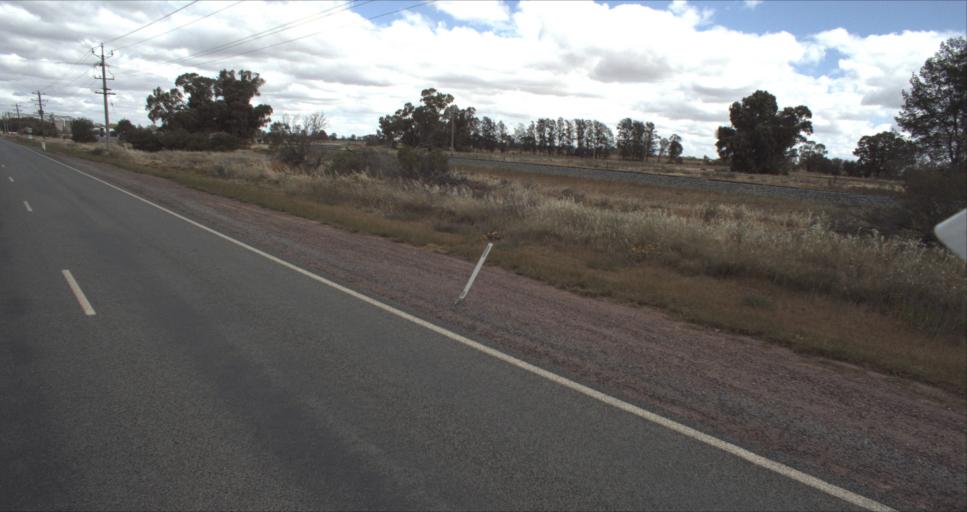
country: AU
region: New South Wales
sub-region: Leeton
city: Leeton
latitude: -34.5947
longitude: 146.4052
